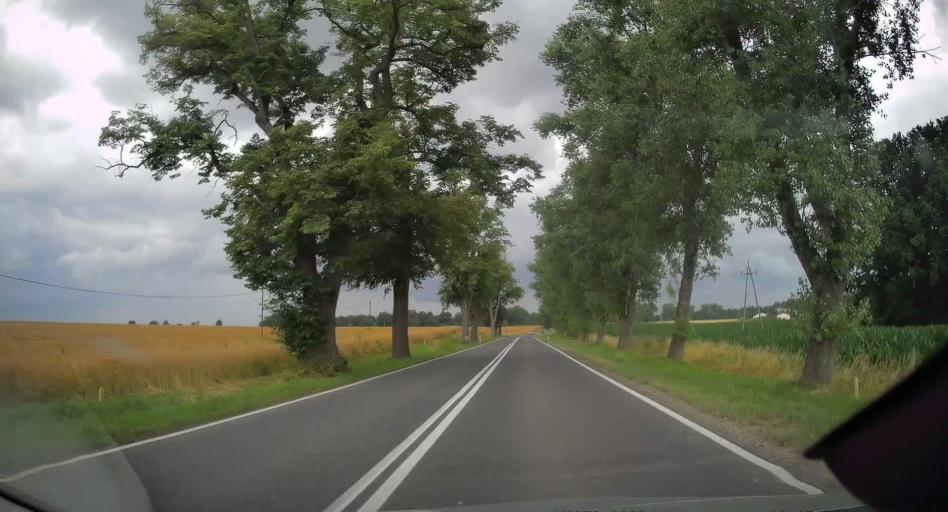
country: PL
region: Opole Voivodeship
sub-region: Powiat prudnicki
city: Laka Prudnicka
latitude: 50.3952
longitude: 17.5101
